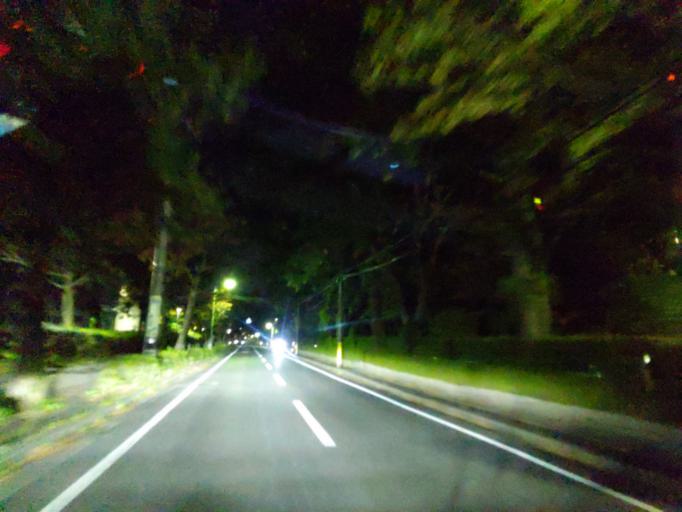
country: JP
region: Okayama
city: Okayama-shi
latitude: 34.6876
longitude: 133.9191
